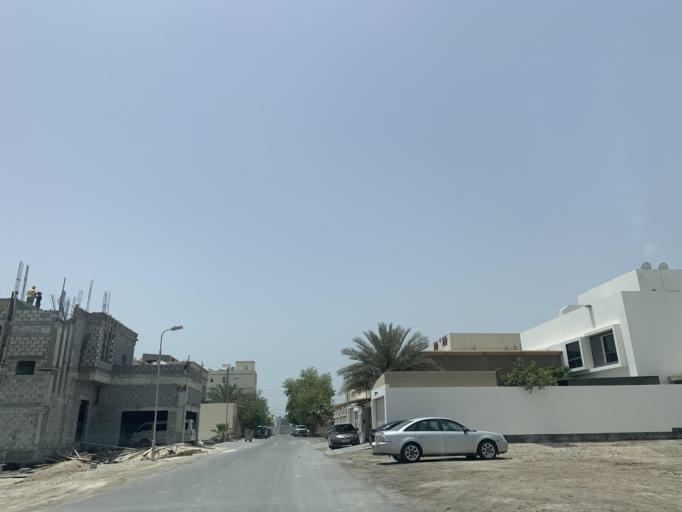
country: BH
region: Northern
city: Sitrah
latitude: 26.1432
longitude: 50.5890
